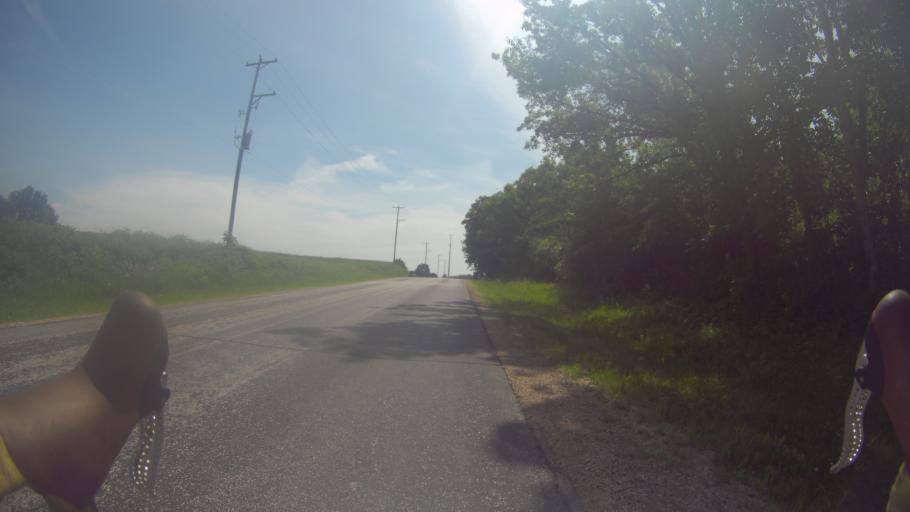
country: US
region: Wisconsin
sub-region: Dane County
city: Deerfield
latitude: 43.0452
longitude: -89.0460
